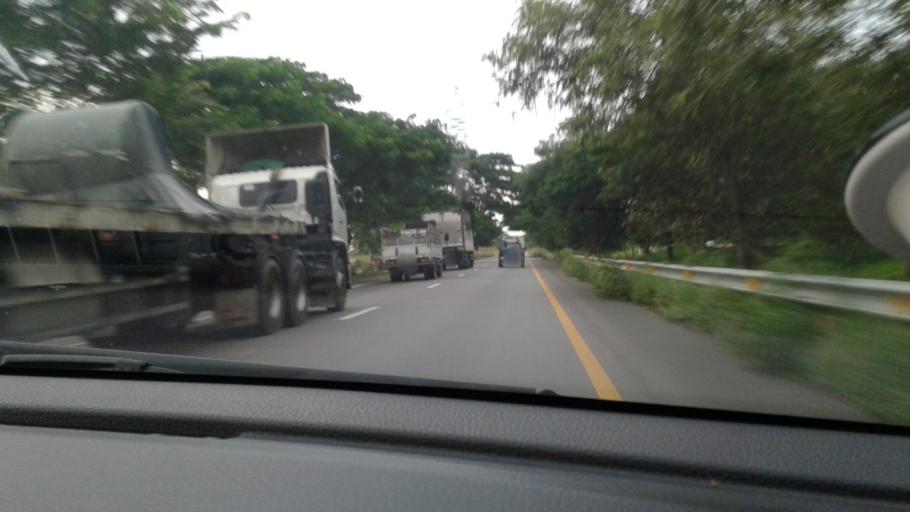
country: TH
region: Prachuap Khiri Khan
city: Hua Hin
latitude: 12.5369
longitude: 99.8768
